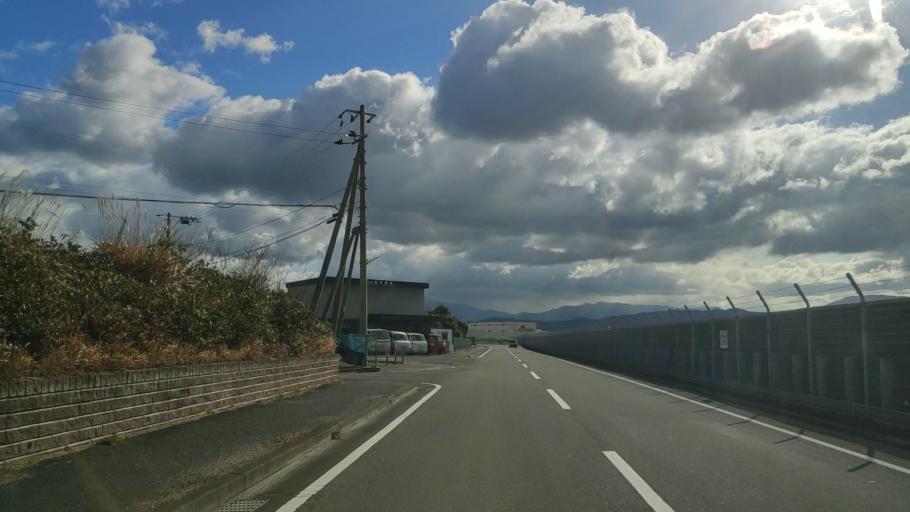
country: JP
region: Ehime
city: Masaki-cho
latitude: 33.8233
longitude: 132.7093
